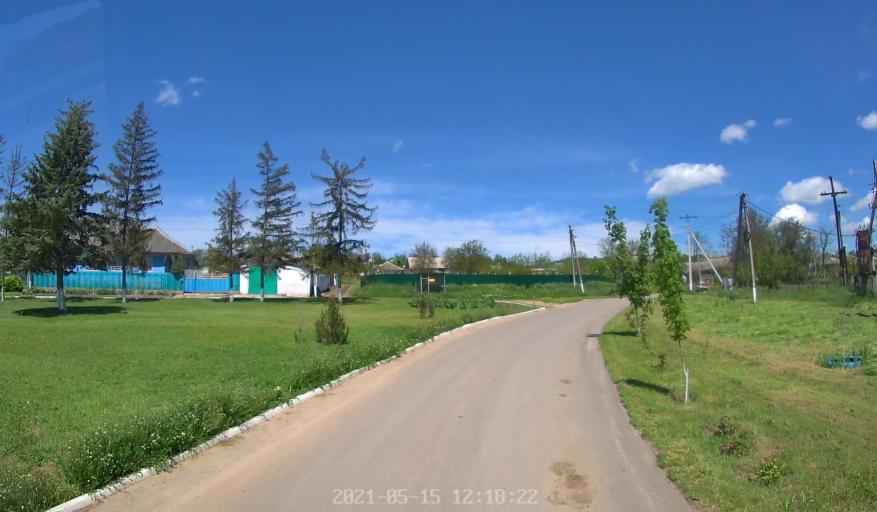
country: MD
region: Hincesti
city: Hincesti
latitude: 46.7973
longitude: 28.5411
